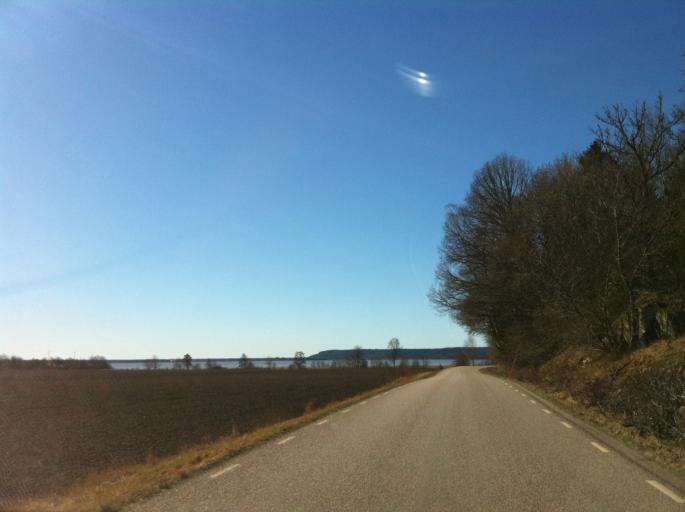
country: SE
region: Vaestra Goetaland
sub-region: Grastorps Kommun
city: Graestorp
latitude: 58.4319
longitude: 12.6116
